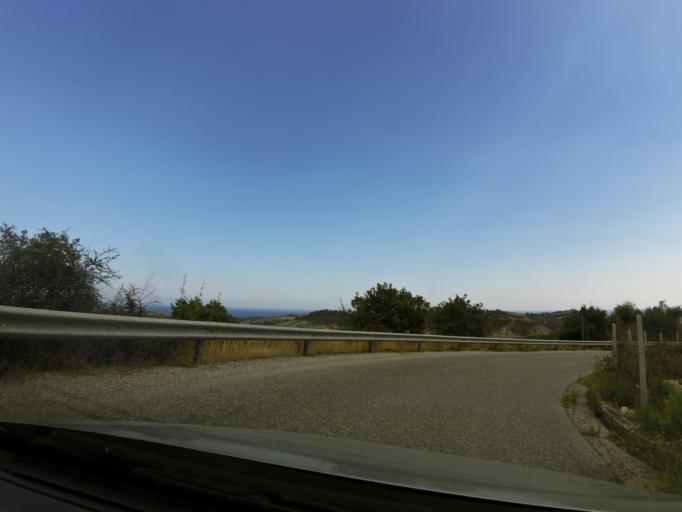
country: IT
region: Calabria
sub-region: Provincia di Reggio Calabria
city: Camini
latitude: 38.4296
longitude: 16.5144
